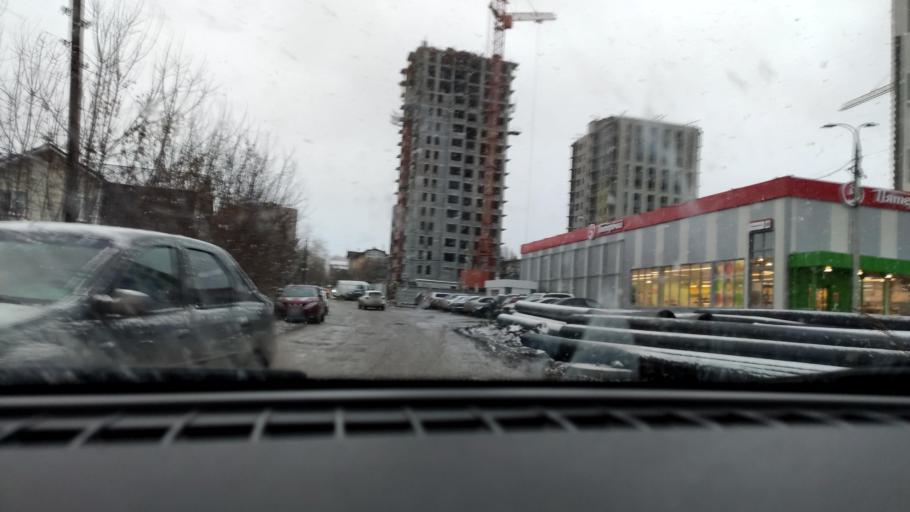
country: RU
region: Perm
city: Perm
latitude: 57.9746
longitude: 56.1863
